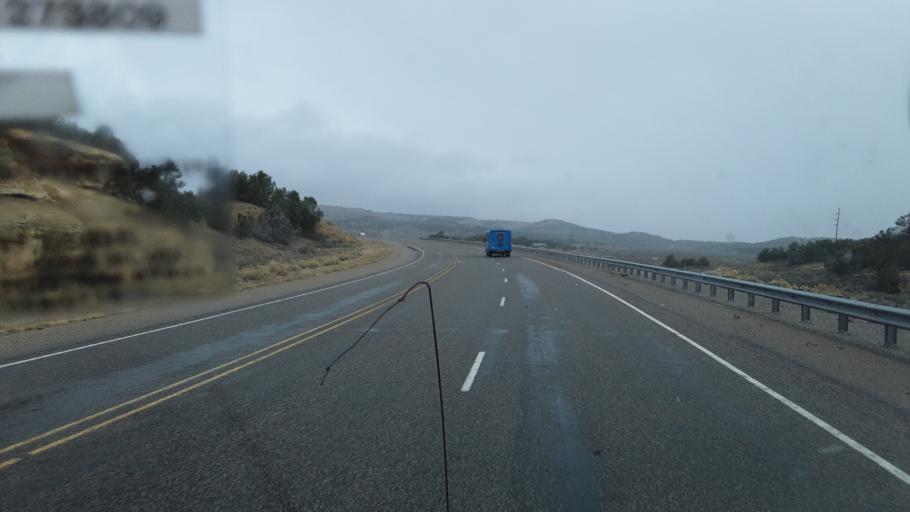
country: US
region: New Mexico
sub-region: Rio Arriba County
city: Tierra Amarilla
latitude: 36.4361
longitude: -106.4741
